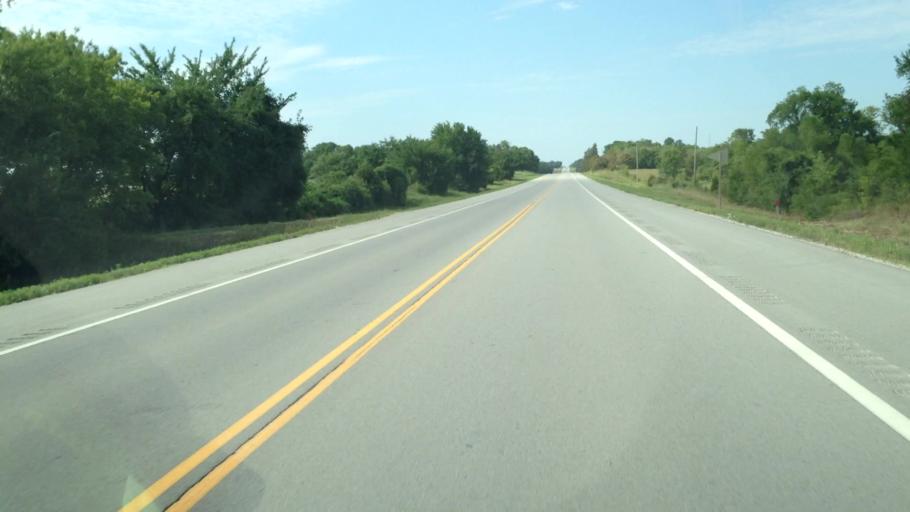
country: US
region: Kansas
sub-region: Labette County
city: Parsons
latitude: 37.2850
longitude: -95.2675
